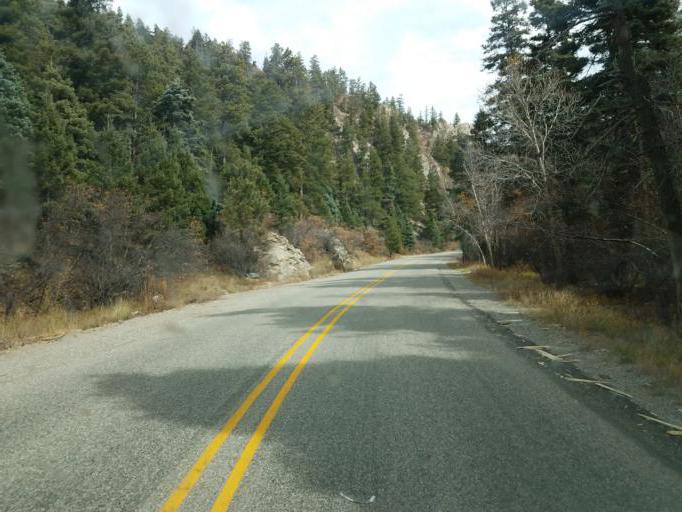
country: US
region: New Mexico
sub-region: Taos County
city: Arroyo Seco
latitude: 36.5686
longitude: -105.5222
